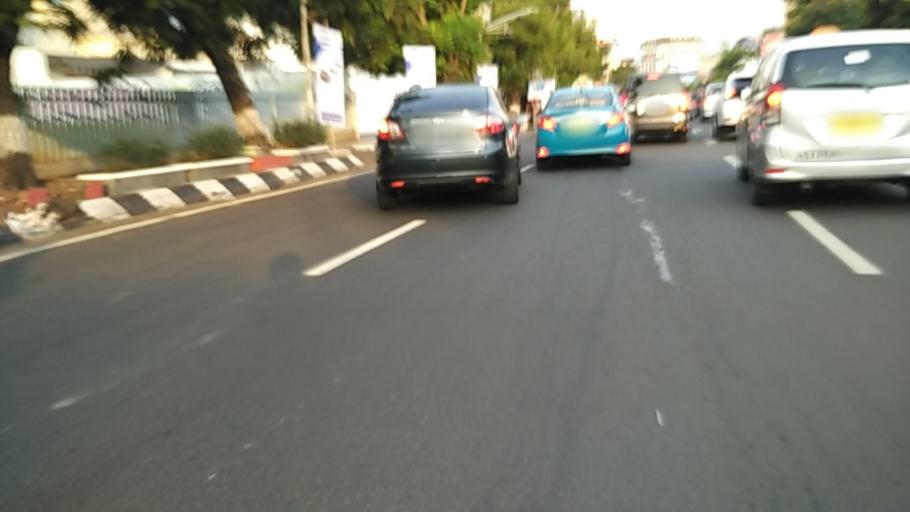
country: ID
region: Central Java
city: Semarang
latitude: -6.9871
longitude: 110.4161
